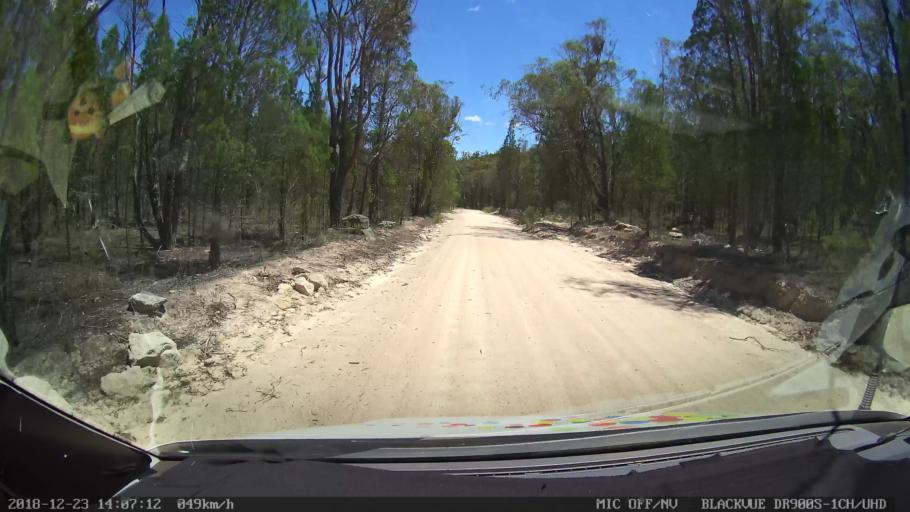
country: AU
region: New South Wales
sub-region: Tamworth Municipality
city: Manilla
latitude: -30.6344
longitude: 151.0728
